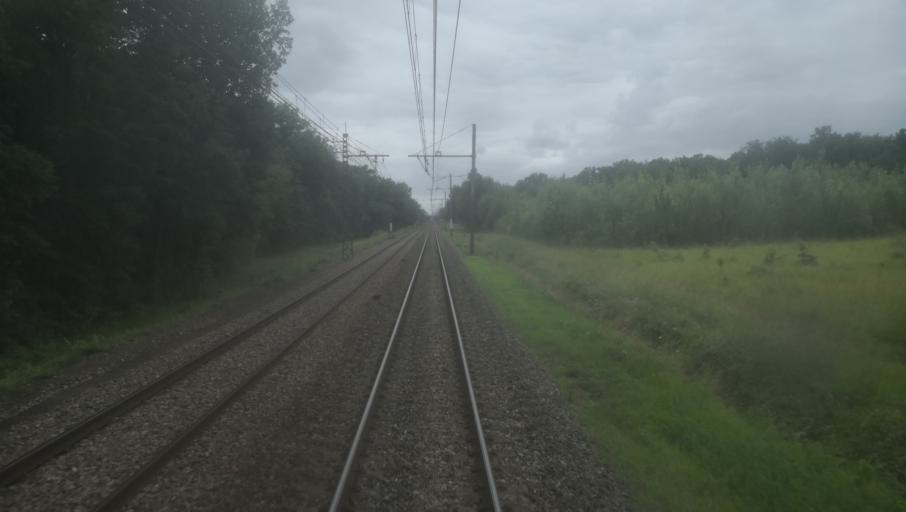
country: FR
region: Midi-Pyrenees
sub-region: Departement du Tarn-et-Garonne
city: Finhan
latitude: 43.8954
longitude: 1.2693
